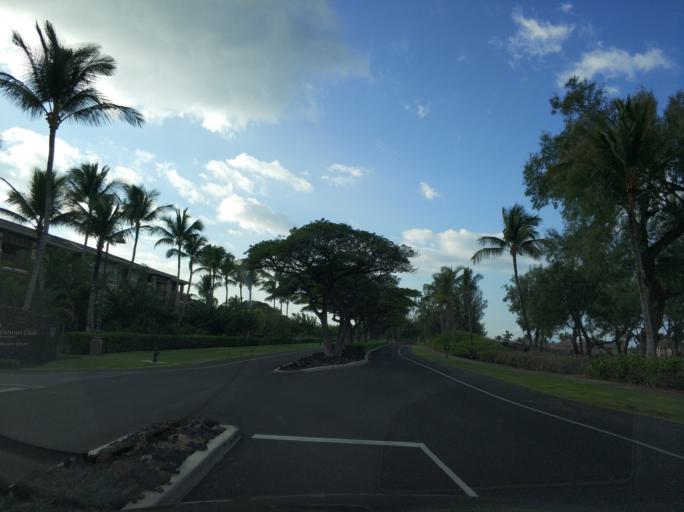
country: US
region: Hawaii
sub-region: Hawaii County
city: Waikoloa Village
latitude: 19.9231
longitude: -155.8774
